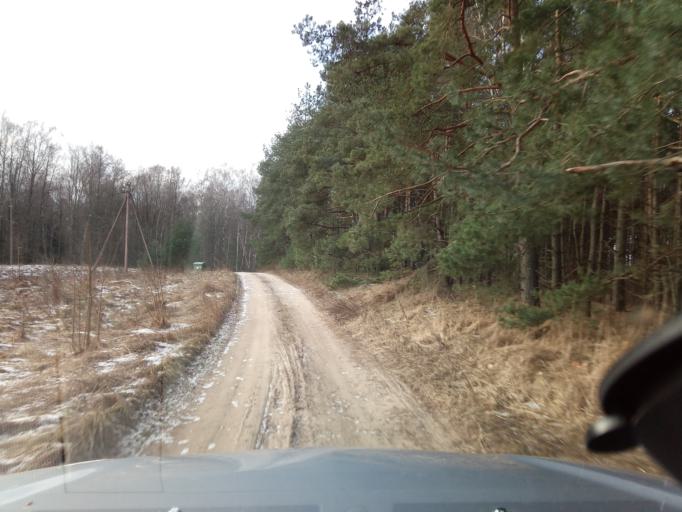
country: LT
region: Alytaus apskritis
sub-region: Alytaus rajonas
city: Daugai
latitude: 54.3776
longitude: 24.4110
